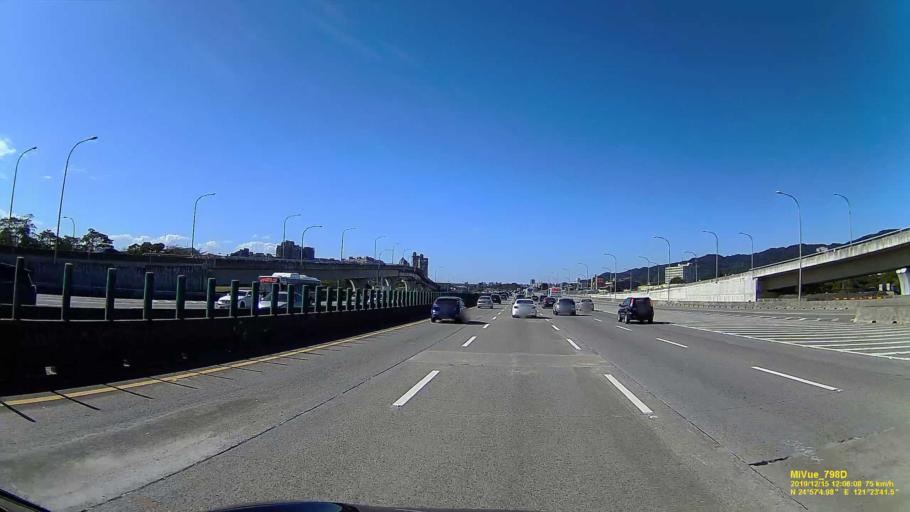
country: TW
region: Taiwan
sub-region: Taoyuan
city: Taoyuan
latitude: 24.9516
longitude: 121.3949
